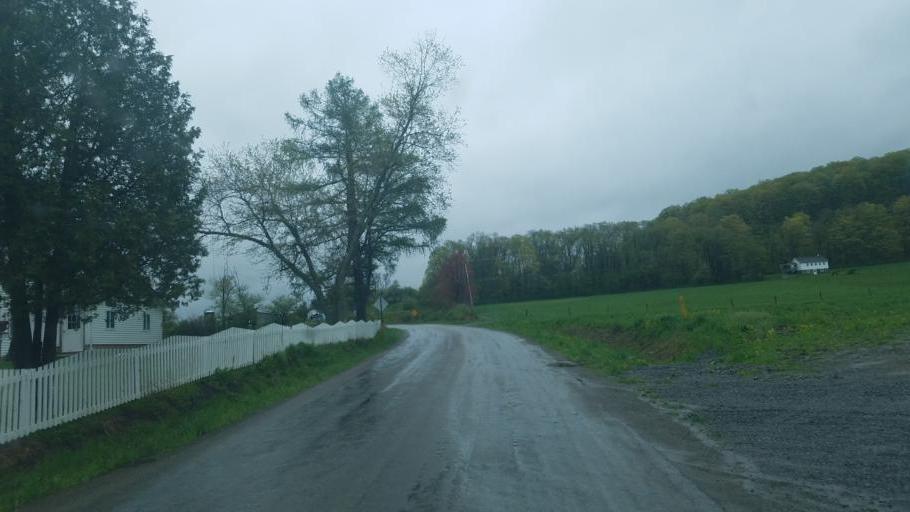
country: US
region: Pennsylvania
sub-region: Potter County
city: Galeton
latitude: 41.9210
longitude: -77.7794
